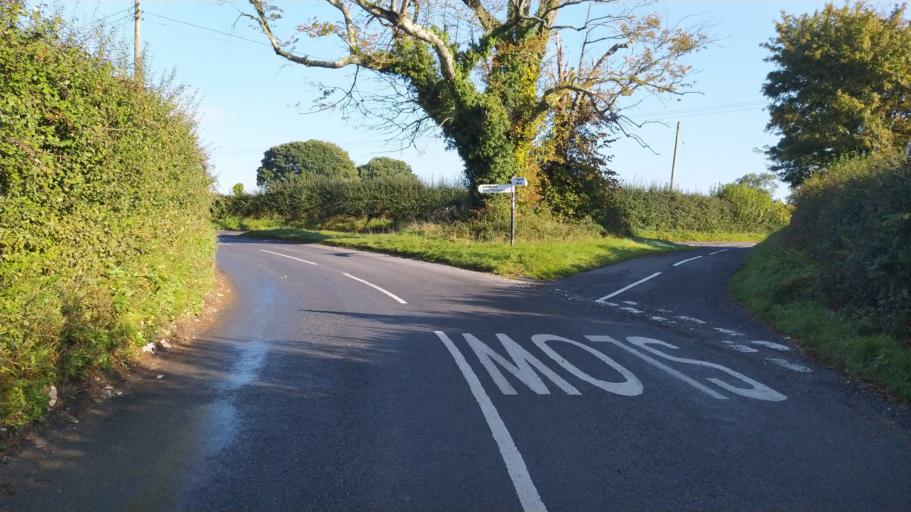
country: GB
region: England
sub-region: Wiltshire
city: Ansty
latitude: 50.9404
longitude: -2.0730
